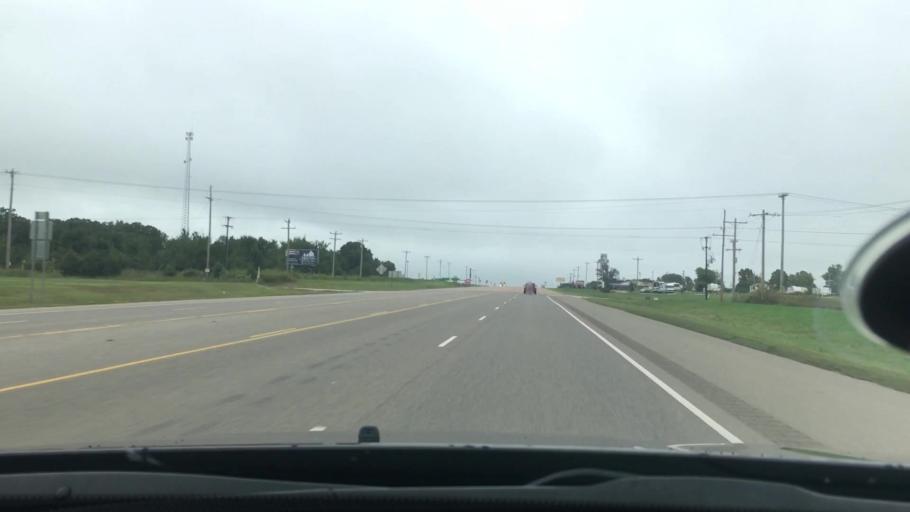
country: US
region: Oklahoma
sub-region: Lincoln County
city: Prague
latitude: 35.3760
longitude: -96.6714
